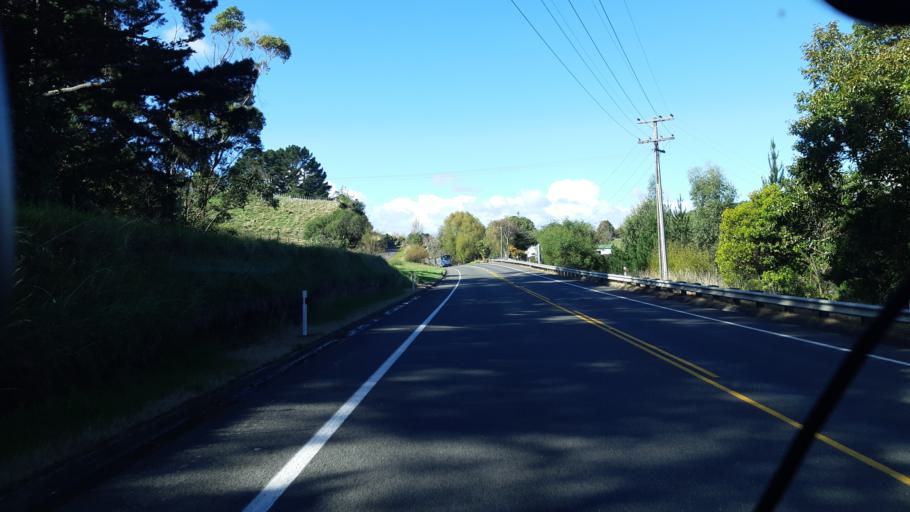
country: NZ
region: Manawatu-Wanganui
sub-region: Wanganui District
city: Wanganui
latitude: -39.9577
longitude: 175.0812
